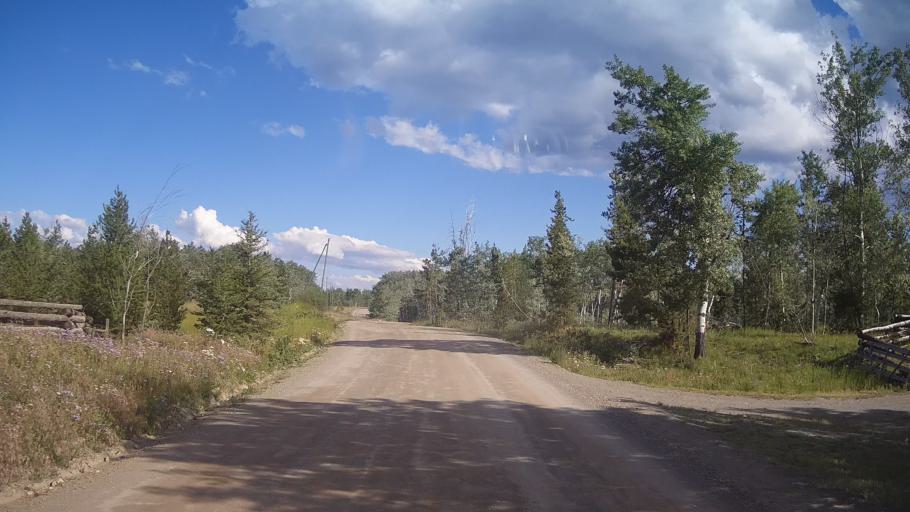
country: CA
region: British Columbia
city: Cache Creek
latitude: 51.2619
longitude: -121.6945
